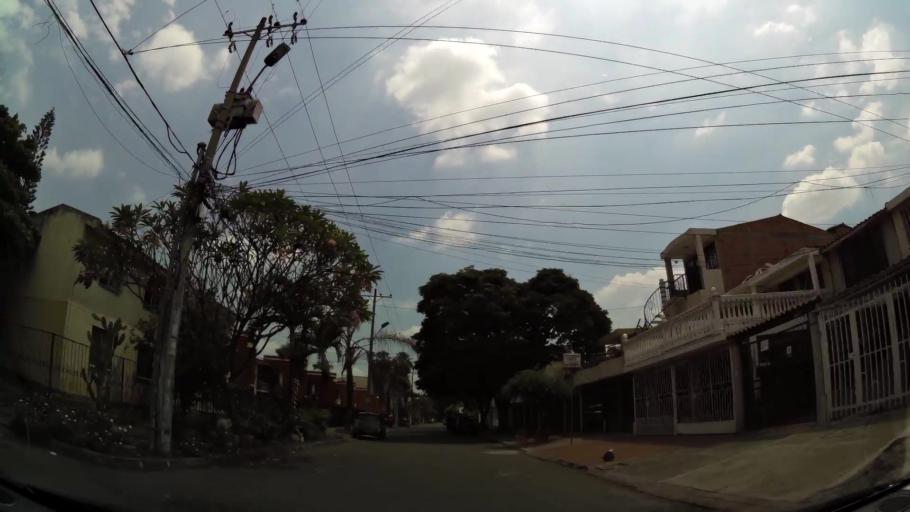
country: CO
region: Valle del Cauca
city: Cali
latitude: 3.4753
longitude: -76.5023
